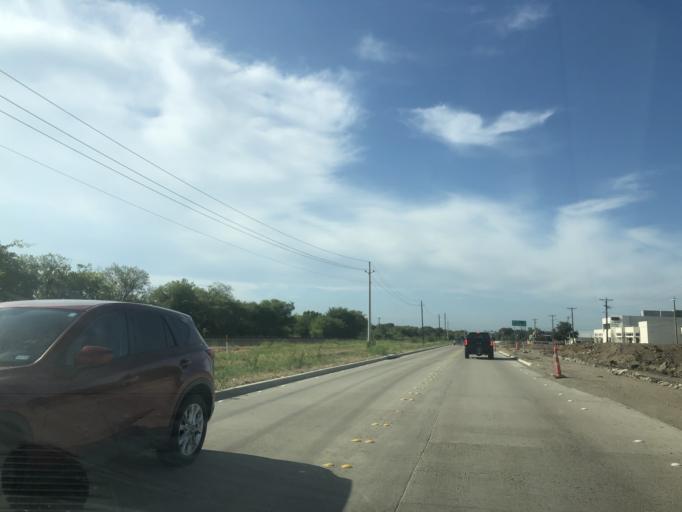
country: US
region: Texas
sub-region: Denton County
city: Justin
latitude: 33.0830
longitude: -97.2959
